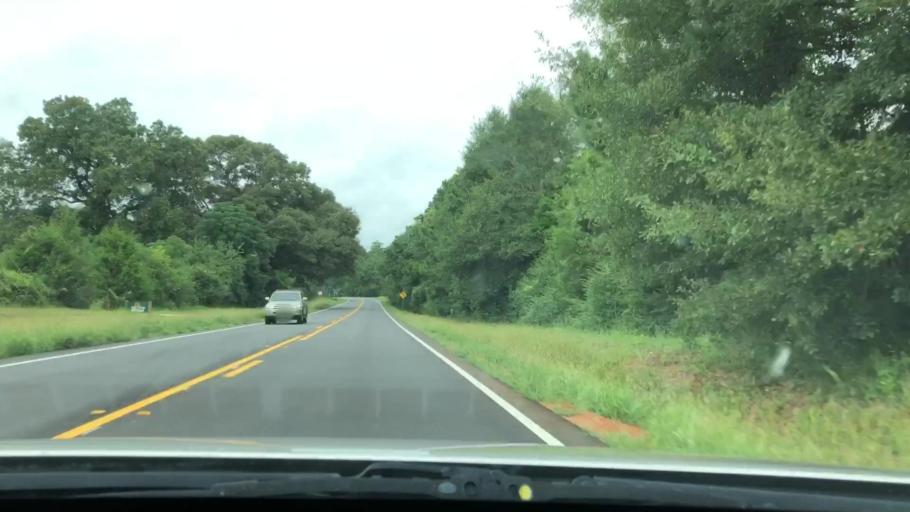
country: US
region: Georgia
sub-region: Upson County
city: Hannahs Mill
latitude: 33.0129
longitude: -84.4746
